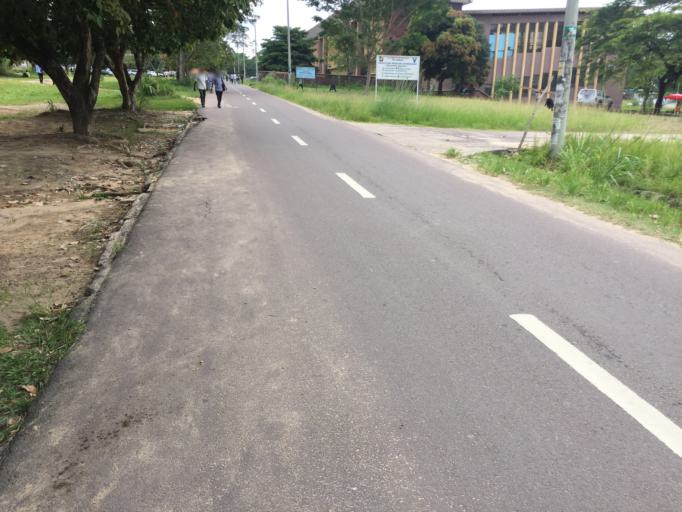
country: CD
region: Kinshasa
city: Kinshasa
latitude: -4.4175
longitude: 15.3075
